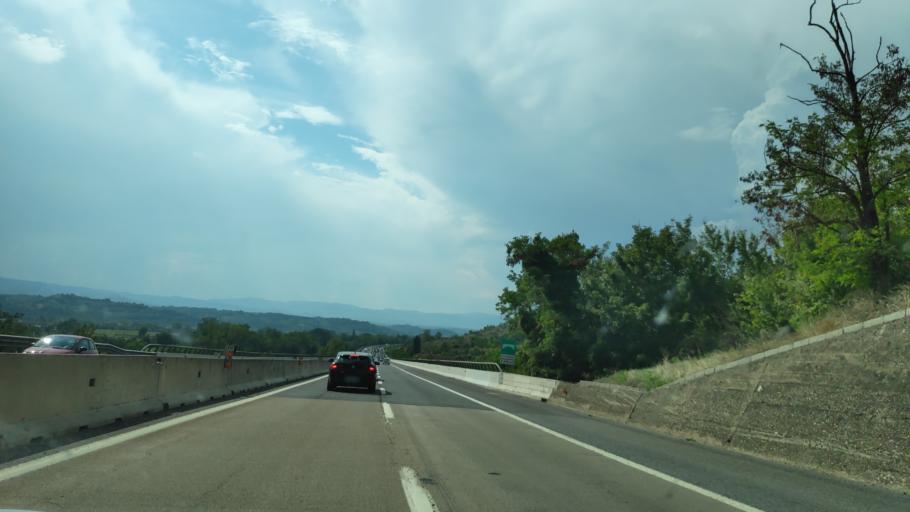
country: IT
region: Tuscany
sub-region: Province of Arezzo
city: Montalto
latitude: 43.5143
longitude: 11.6278
